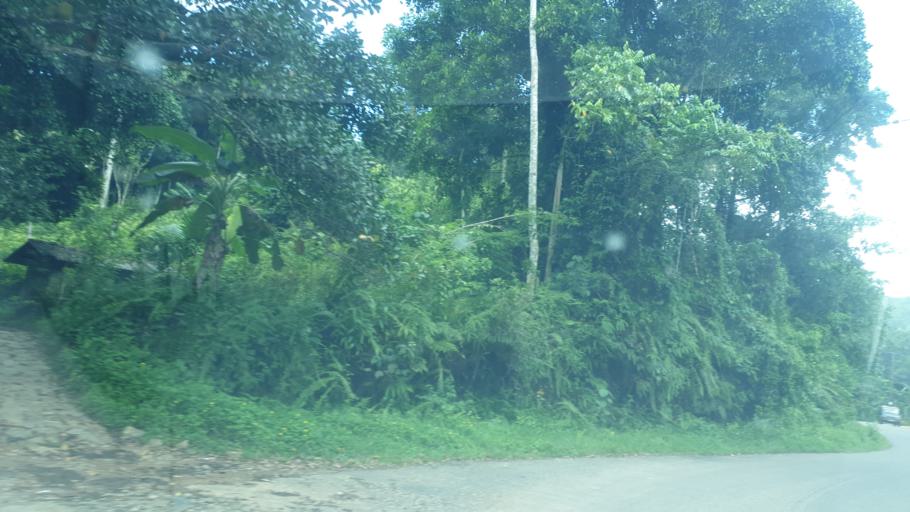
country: LK
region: Sabaragamuwa
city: Ratnapura
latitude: 6.4788
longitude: 80.4167
